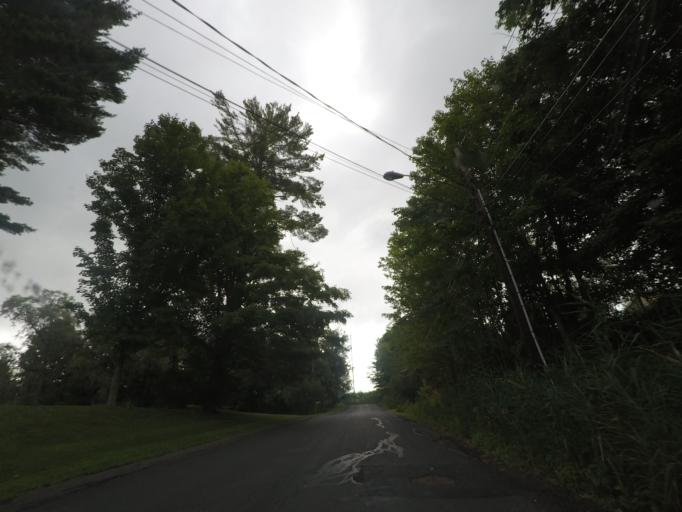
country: US
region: Massachusetts
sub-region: Berkshire County
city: Pittsfield
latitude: 42.4221
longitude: -73.3073
